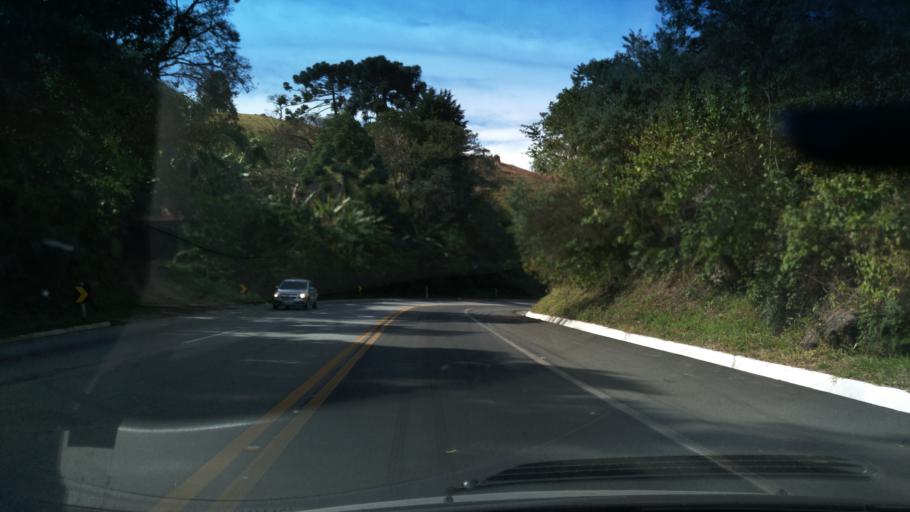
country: BR
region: Minas Gerais
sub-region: Borda Da Mata
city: Borda da Mata
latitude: -22.1308
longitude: -46.1748
